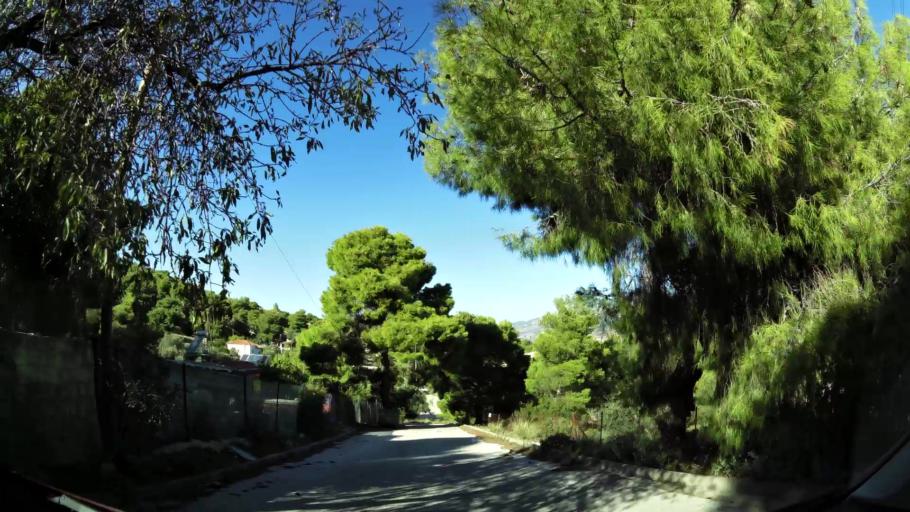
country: GR
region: Attica
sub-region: Nomarchia Anatolikis Attikis
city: Leondarion
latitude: 37.9876
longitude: 23.8418
